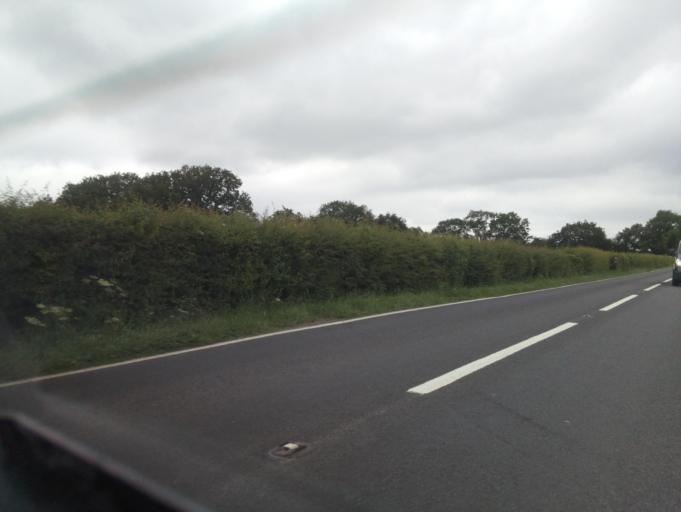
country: GB
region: England
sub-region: Staffordshire
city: Mayfield
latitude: 52.9701
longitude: -1.7525
